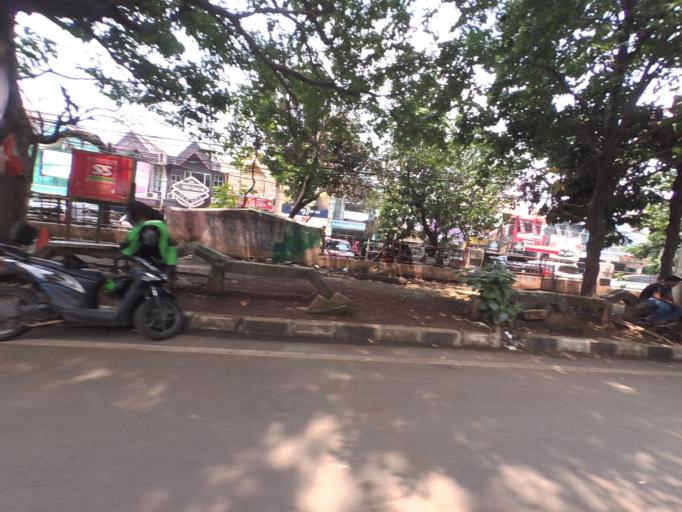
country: ID
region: West Java
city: Bogor
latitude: -6.5620
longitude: 106.7662
